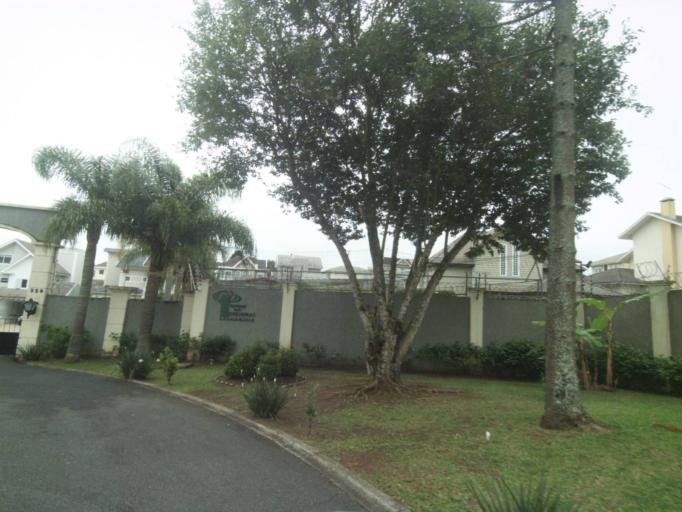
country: BR
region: Parana
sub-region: Curitiba
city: Curitiba
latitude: -25.4250
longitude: -49.3447
